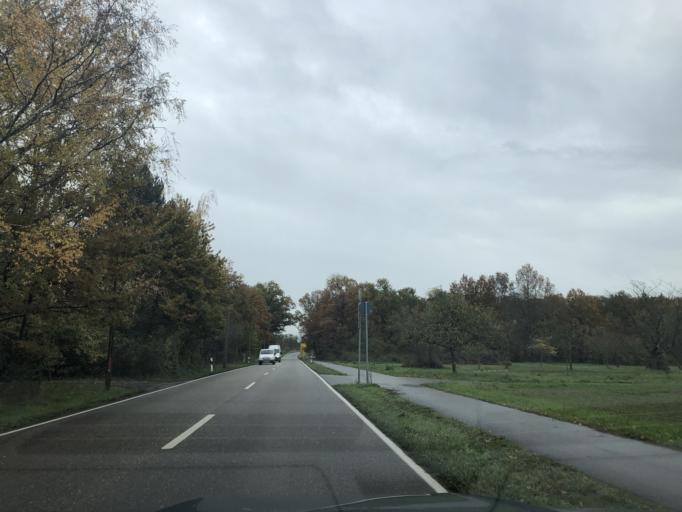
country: DE
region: Rheinland-Pfalz
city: Bellheim
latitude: 49.1879
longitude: 8.3022
